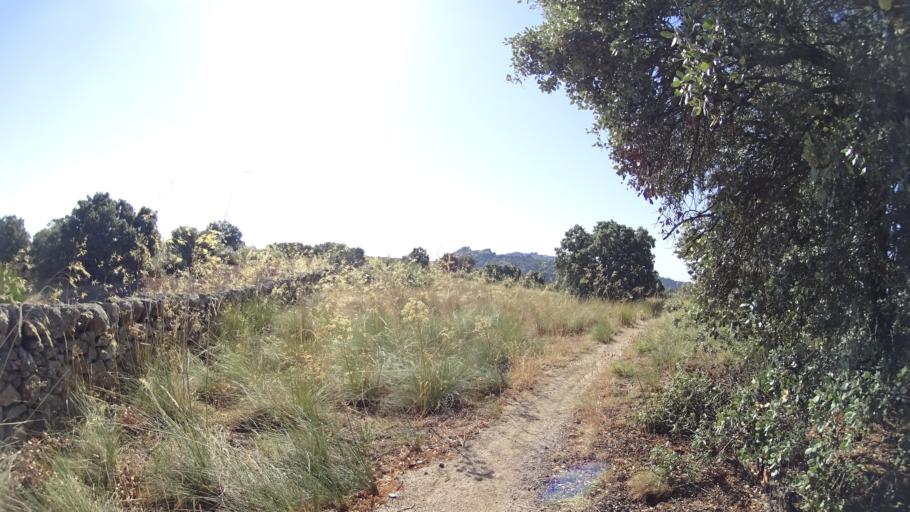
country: ES
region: Madrid
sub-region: Provincia de Madrid
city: Hoyo de Manzanares
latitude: 40.6495
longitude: -3.9390
